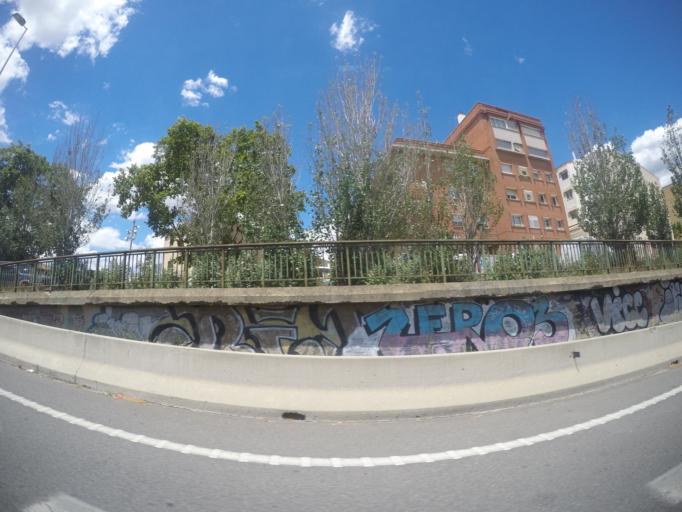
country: ES
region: Catalonia
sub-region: Provincia de Barcelona
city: Badalona
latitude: 41.4545
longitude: 2.2445
